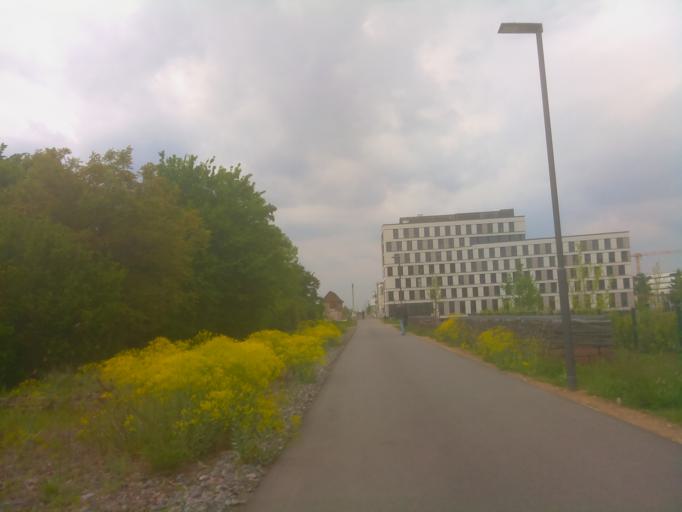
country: DE
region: Baden-Wuerttemberg
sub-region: Karlsruhe Region
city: Heidelberg
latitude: 49.3967
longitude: 8.6745
